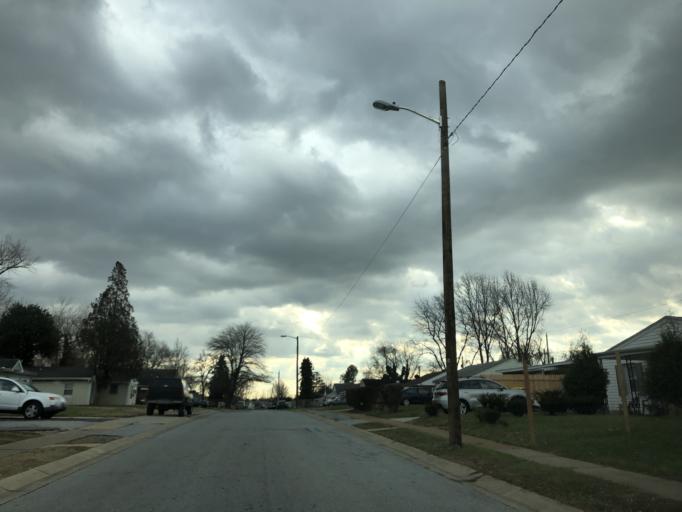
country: US
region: Delaware
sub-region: New Castle County
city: Wilmington Manor
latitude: 39.7081
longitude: -75.5557
